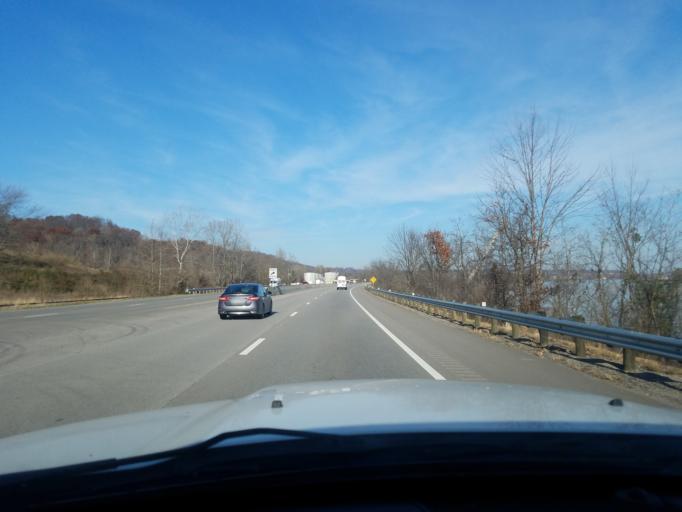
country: US
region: West Virginia
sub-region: Wood County
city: Vienna
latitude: 39.3387
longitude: -81.5595
